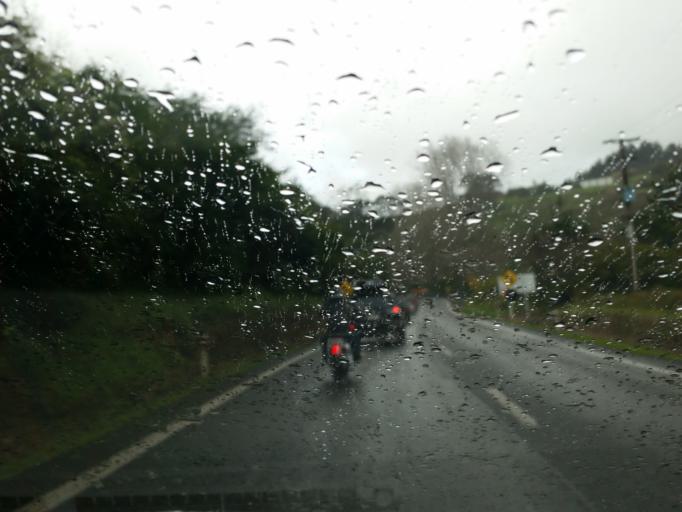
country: NZ
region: Waikato
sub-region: Hauraki District
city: Waihi
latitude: -37.4166
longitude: 175.7582
